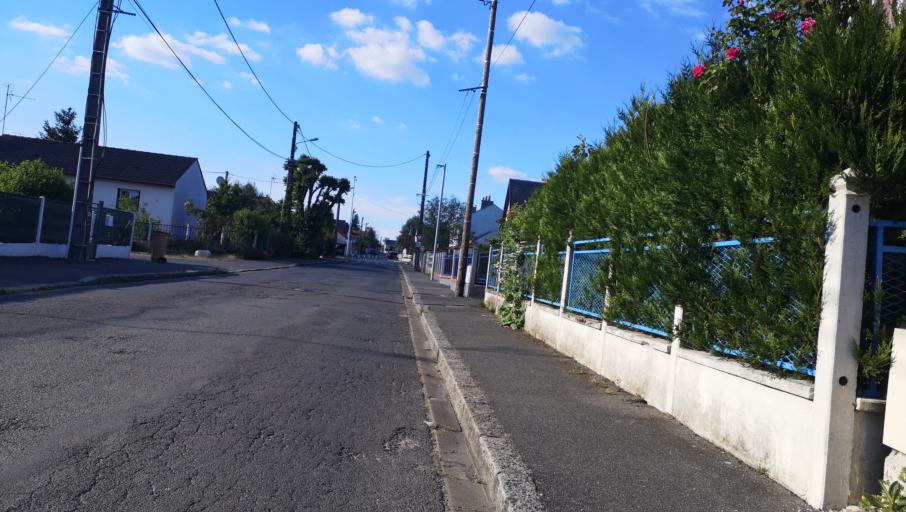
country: FR
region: Centre
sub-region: Departement du Loiret
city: Semoy
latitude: 47.9195
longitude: 1.9376
